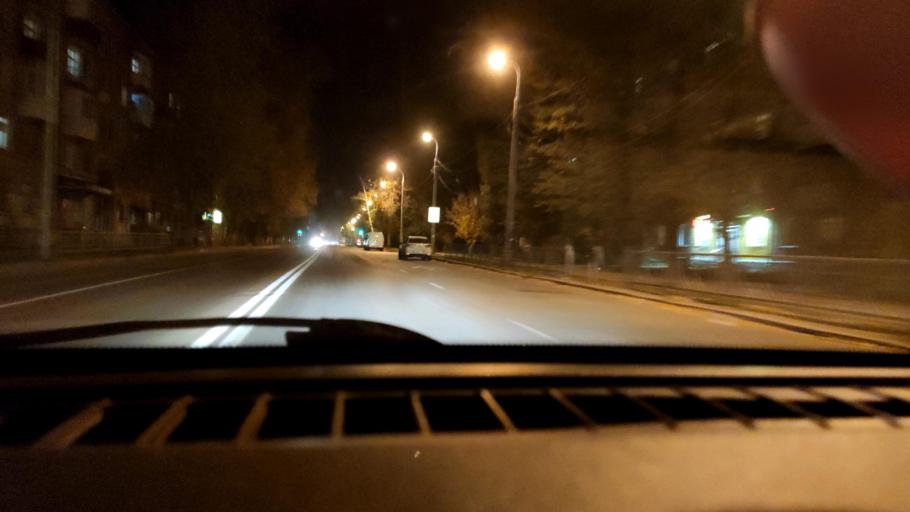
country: RU
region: Samara
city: Samara
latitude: 53.2117
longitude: 50.2509
